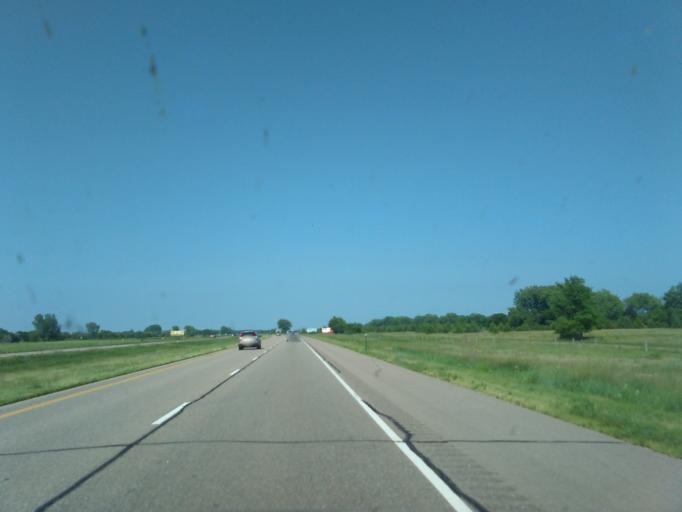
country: US
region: Nebraska
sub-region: Hall County
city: Wood River
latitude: 40.7393
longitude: -98.6363
